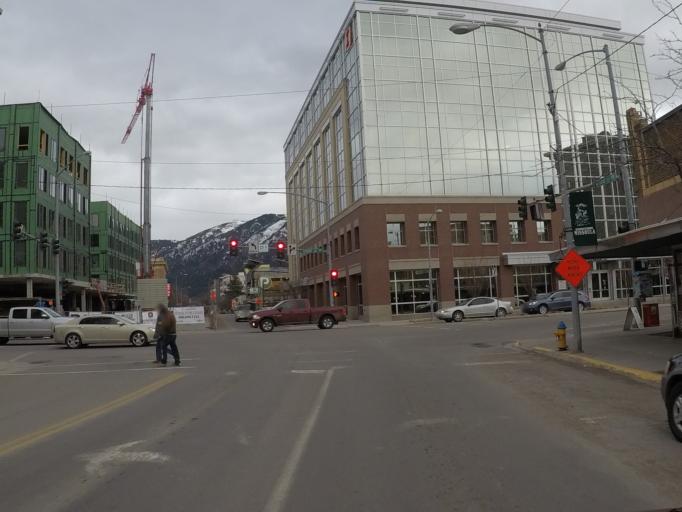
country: US
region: Montana
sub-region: Missoula County
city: Missoula
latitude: 46.8702
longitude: -113.9957
